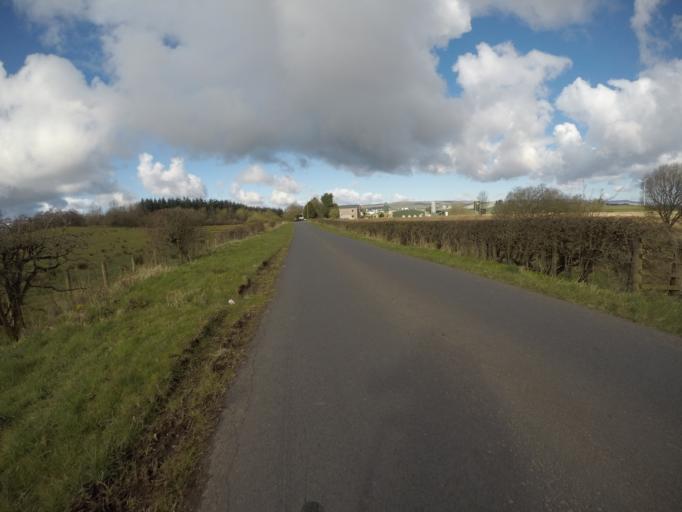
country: GB
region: Scotland
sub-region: North Ayrshire
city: Kilwinning
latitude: 55.6855
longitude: -4.6529
